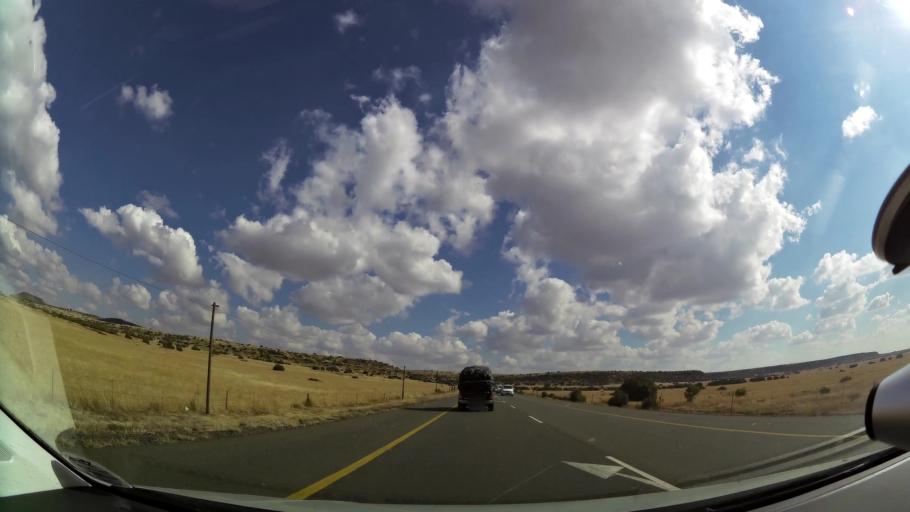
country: ZA
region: Orange Free State
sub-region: Mangaung Metropolitan Municipality
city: Bloemfontein
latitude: -29.1478
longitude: 26.0701
